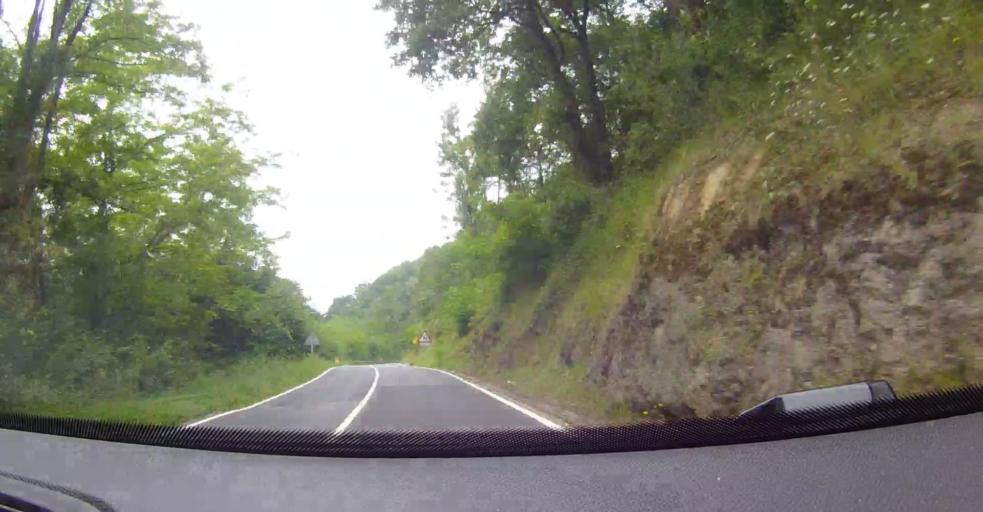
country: ES
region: Basque Country
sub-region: Bizkaia
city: Lanestosa
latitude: 43.2410
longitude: -3.3582
